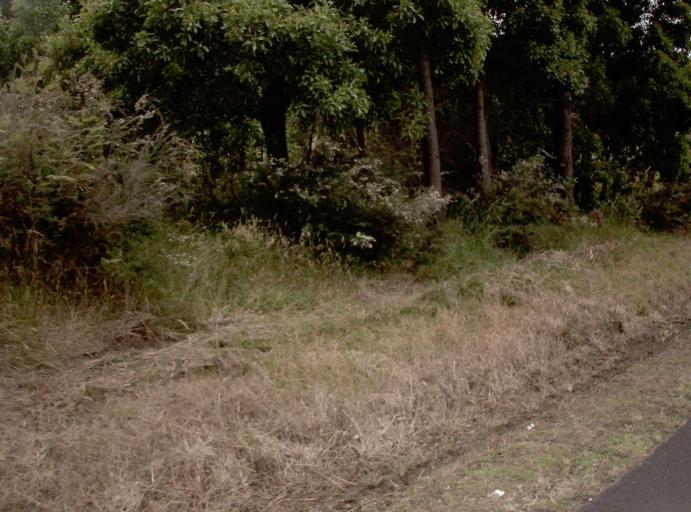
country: AU
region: Victoria
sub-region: Wellington
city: Sale
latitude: -38.2176
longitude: 147.0603
